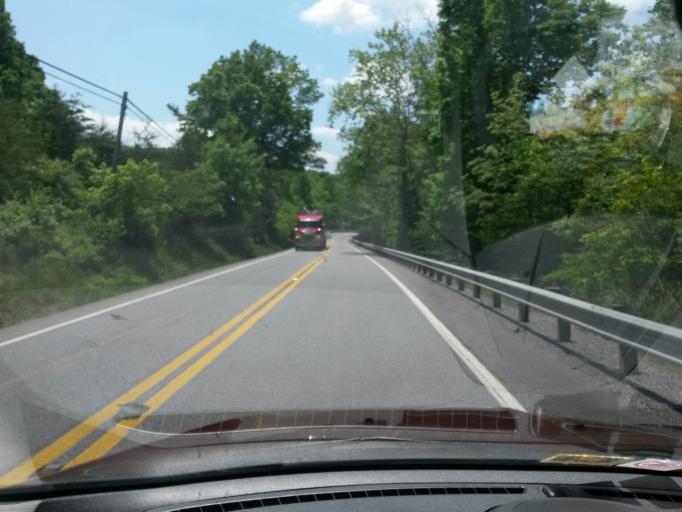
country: US
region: Virginia
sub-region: Alleghany County
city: Clifton Forge
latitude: 37.7190
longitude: -79.8073
